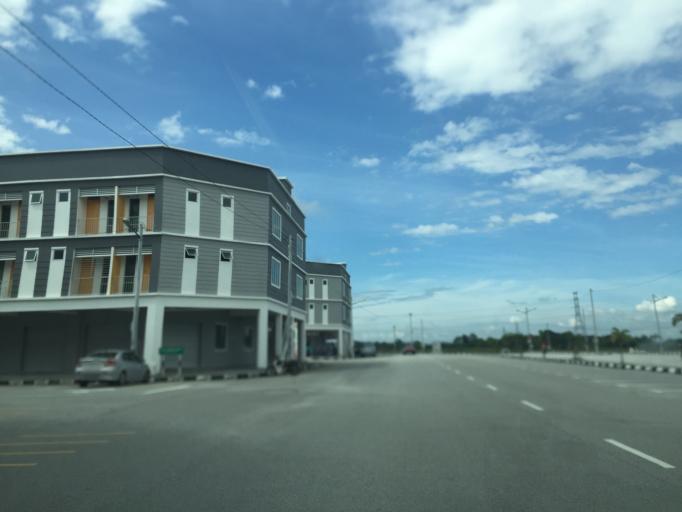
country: MY
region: Perak
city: Kampar
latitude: 4.3227
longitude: 101.1269
